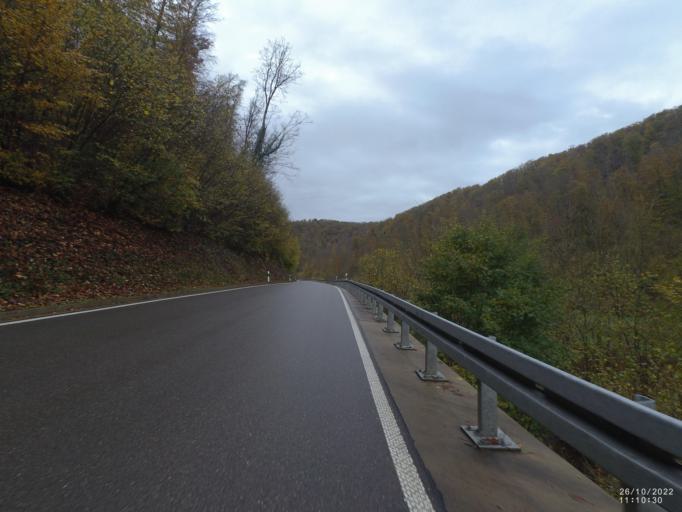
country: DE
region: Baden-Wuerttemberg
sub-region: Regierungsbezirk Stuttgart
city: Bohmenkirch
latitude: 48.6627
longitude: 9.8943
